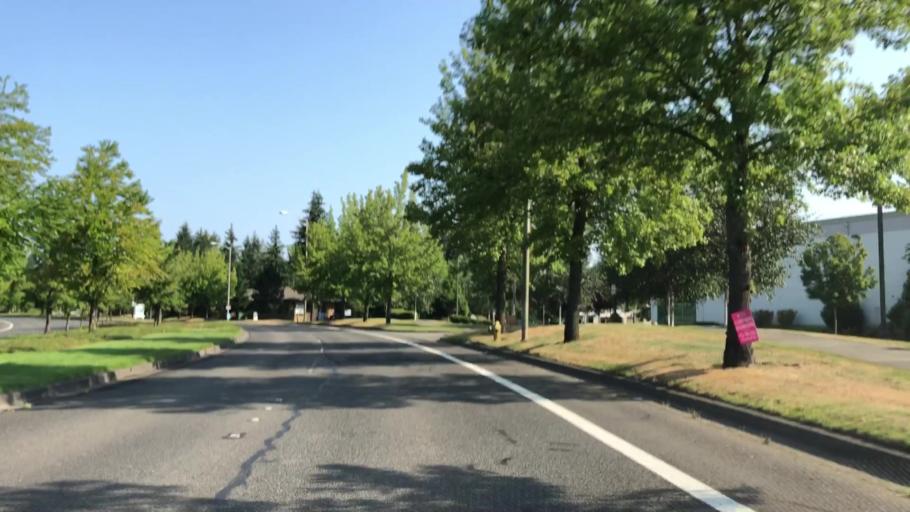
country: US
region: Washington
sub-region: Thurston County
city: Tanglewilde-Thompson Place
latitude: 47.0746
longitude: -122.7501
